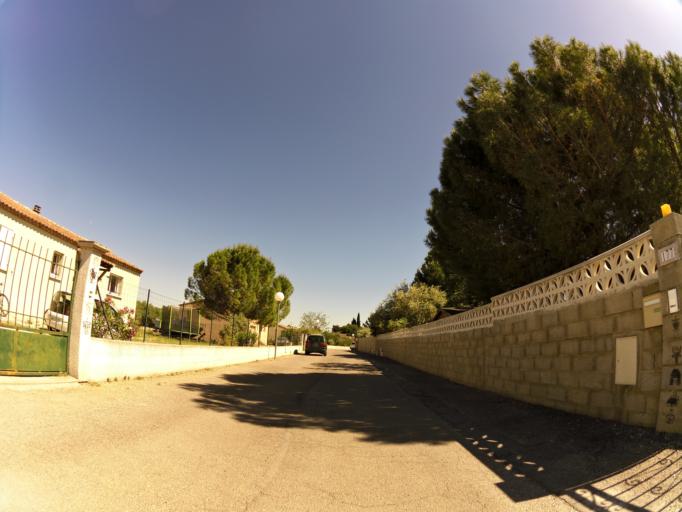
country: FR
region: Languedoc-Roussillon
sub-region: Departement de l'Herault
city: Villetelle
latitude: 43.7343
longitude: 4.1362
